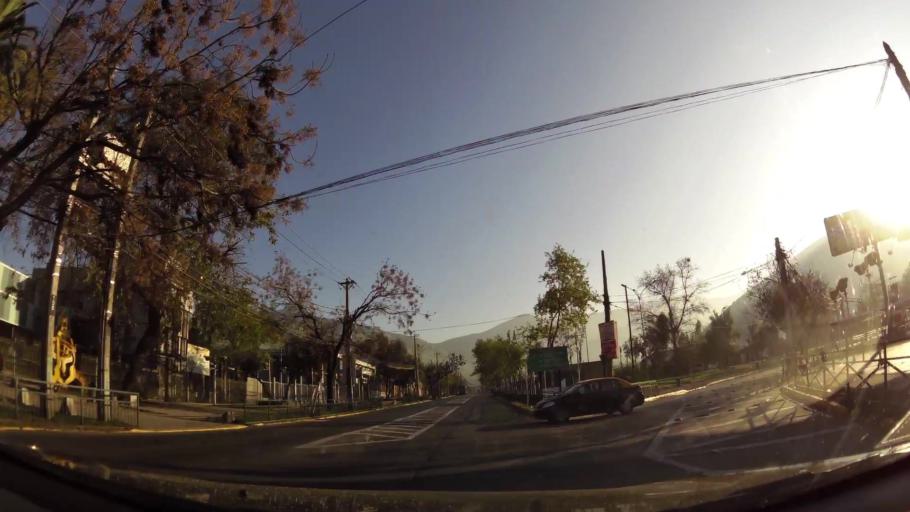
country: CL
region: Santiago Metropolitan
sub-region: Provincia de Santiago
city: Santiago
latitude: -33.3742
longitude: -70.6368
